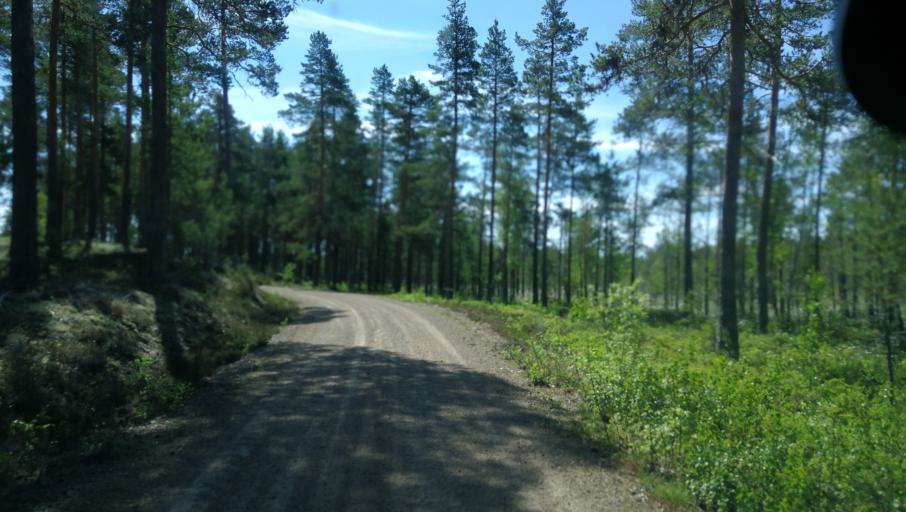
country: SE
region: Dalarna
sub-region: Vansbro Kommun
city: Vansbro
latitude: 60.8227
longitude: 14.1904
